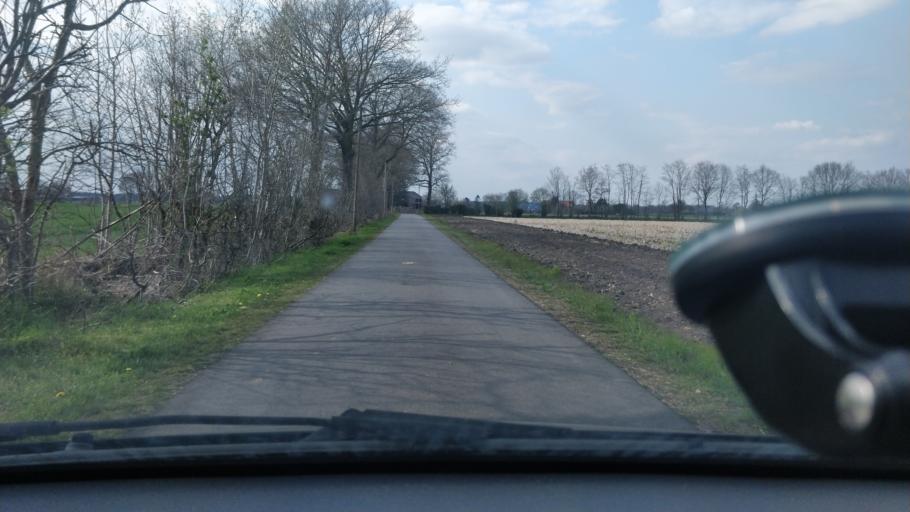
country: DE
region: North Rhine-Westphalia
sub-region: Regierungsbezirk Dusseldorf
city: Bocholt
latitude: 51.8878
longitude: 6.6333
